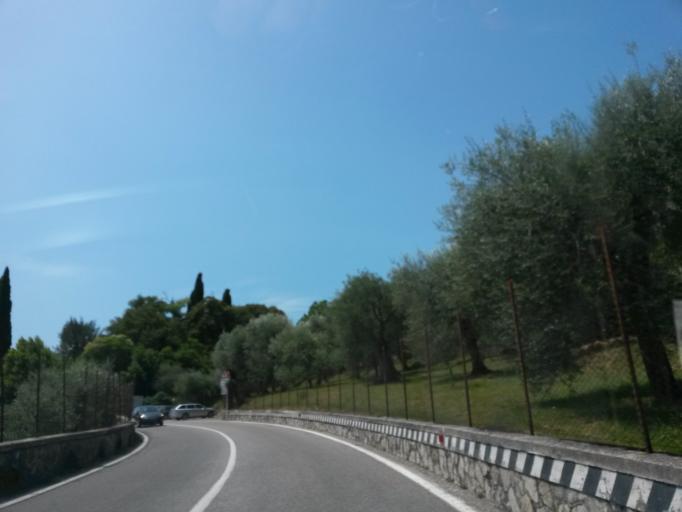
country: IT
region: Lombardy
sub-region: Provincia di Brescia
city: Gargnano
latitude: 45.6938
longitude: 10.6675
